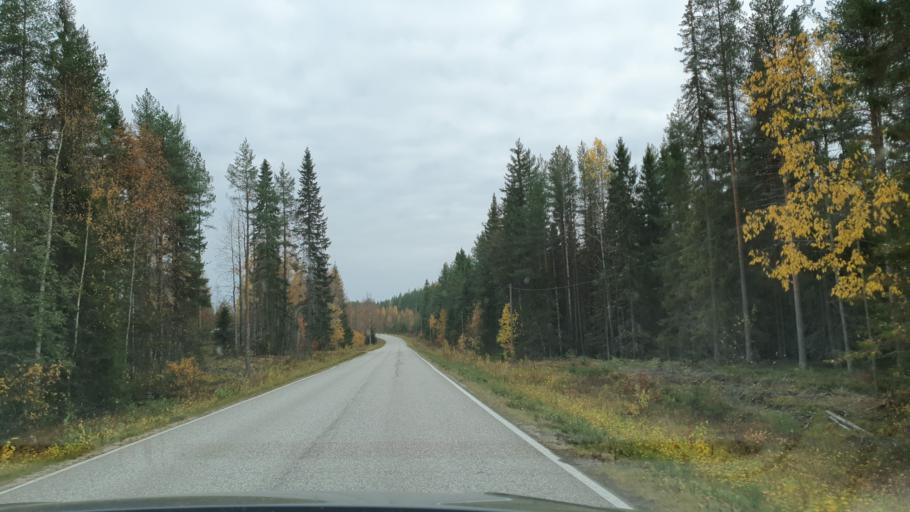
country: FI
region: Kainuu
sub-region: Kajaani
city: Ristijaervi
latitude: 64.4487
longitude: 28.3613
